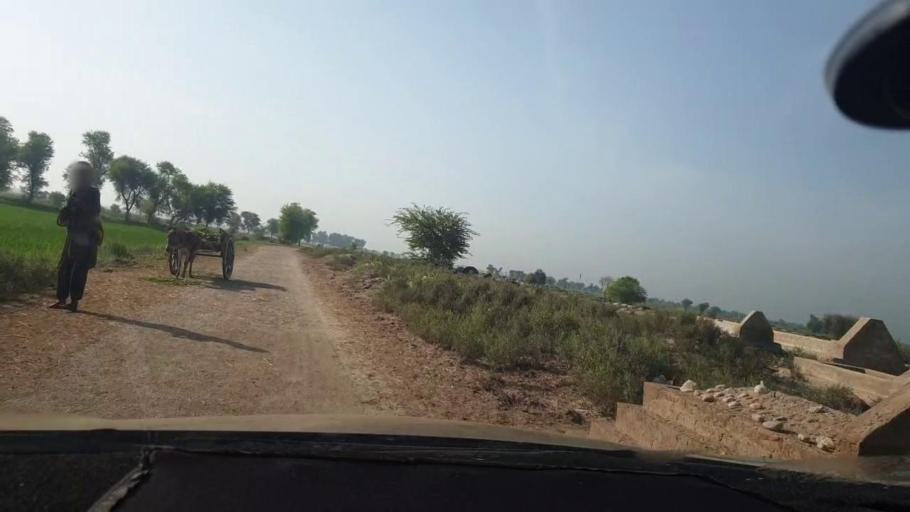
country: PK
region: Sindh
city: Kambar
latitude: 27.6434
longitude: 68.0431
